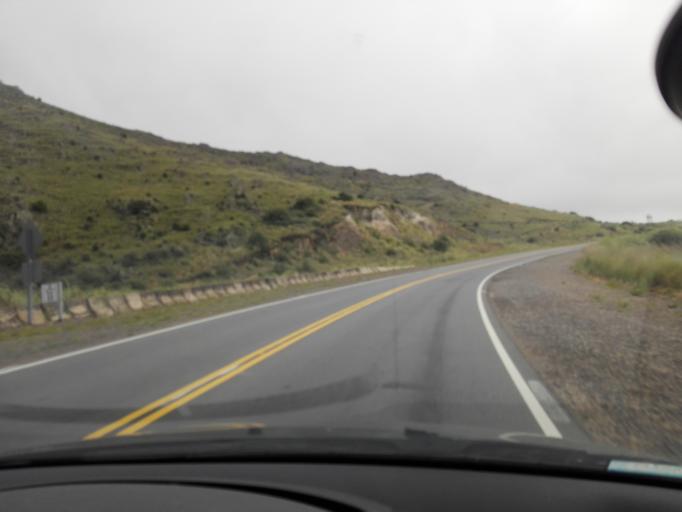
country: AR
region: Cordoba
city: Cuesta Blanca
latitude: -31.6197
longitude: -64.6873
